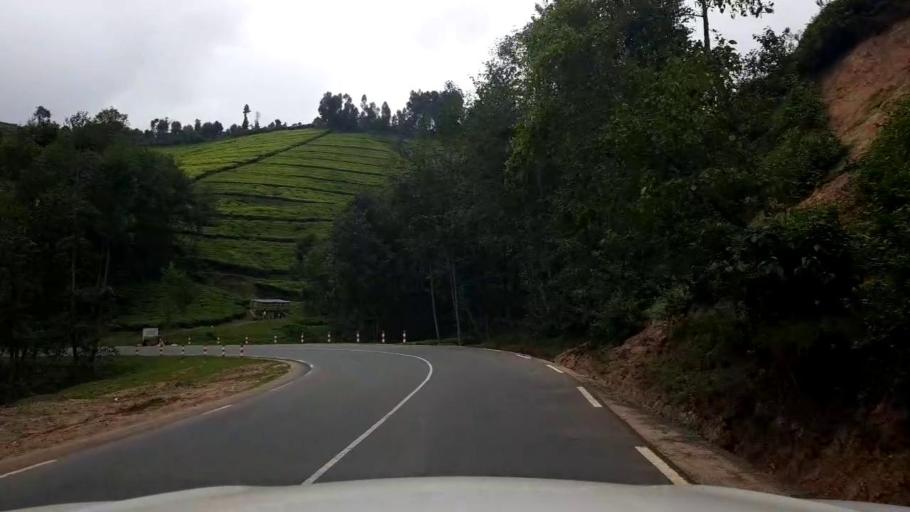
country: RW
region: Northern Province
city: Musanze
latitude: -1.6551
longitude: 29.5096
